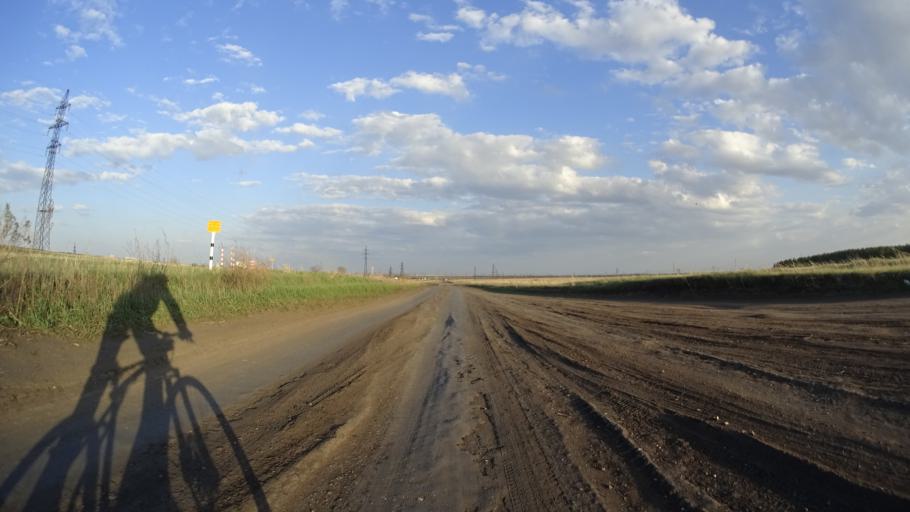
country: RU
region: Chelyabinsk
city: Troitsk
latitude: 54.0505
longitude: 61.5940
